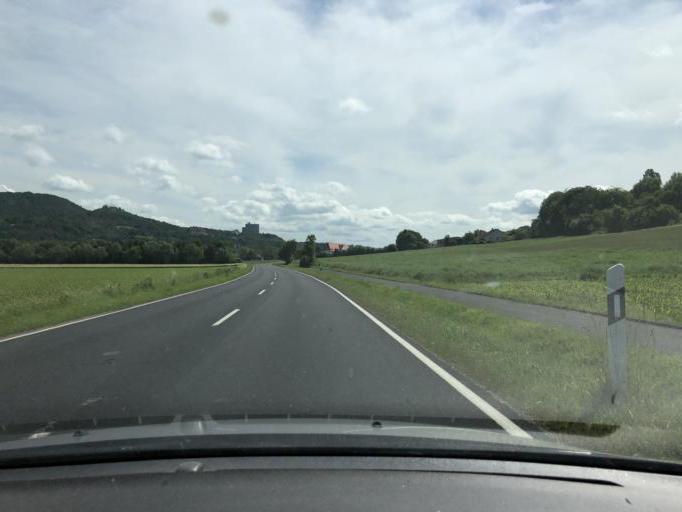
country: DE
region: Hesse
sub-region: Regierungsbezirk Kassel
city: Rotenburg an der Fulda
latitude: 51.0017
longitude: 9.7046
